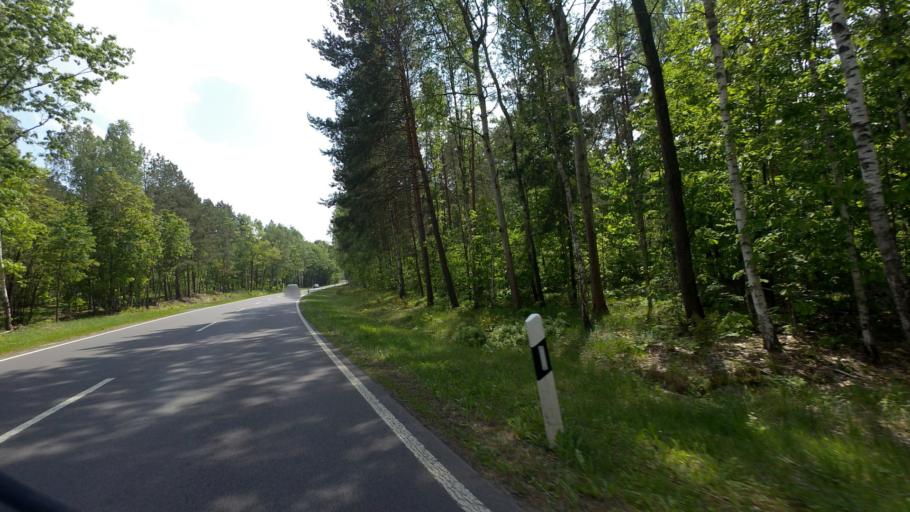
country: DE
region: Saxony
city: Trebendorf
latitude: 51.5329
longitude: 14.5968
